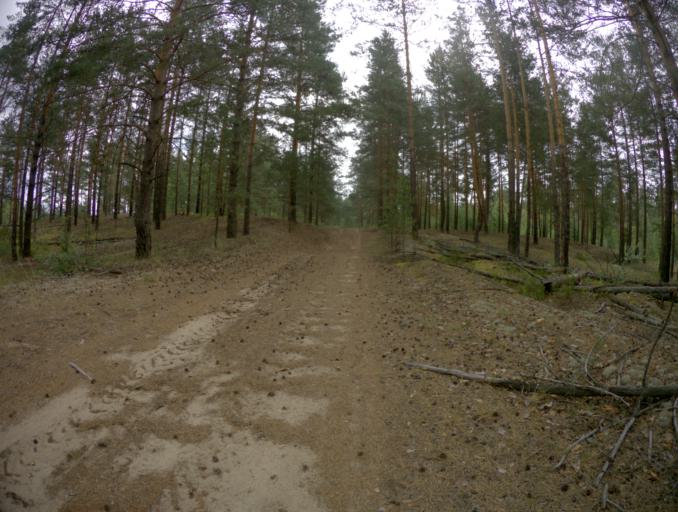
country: RU
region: Nizjnij Novgorod
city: Frolishchi
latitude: 56.3554
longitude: 42.6418
